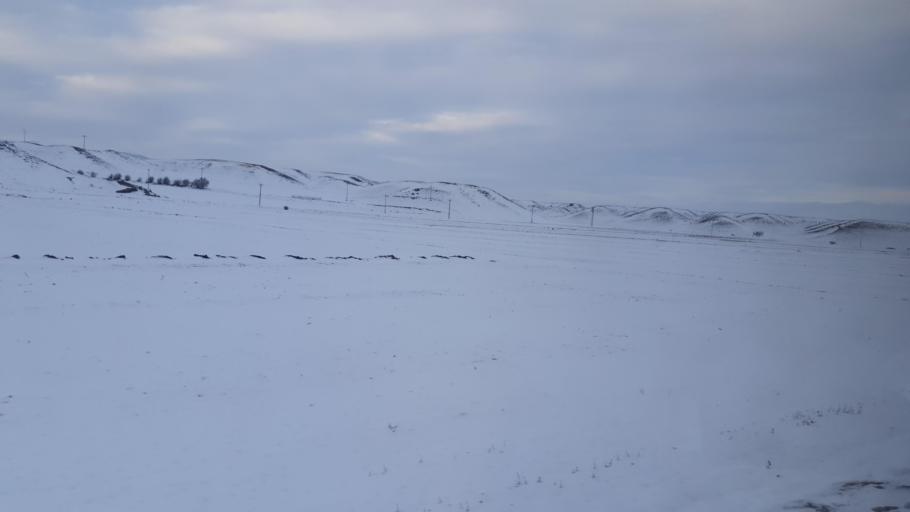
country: TR
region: Kirsehir
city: Mecidiye
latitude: 39.6876
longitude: 34.3910
